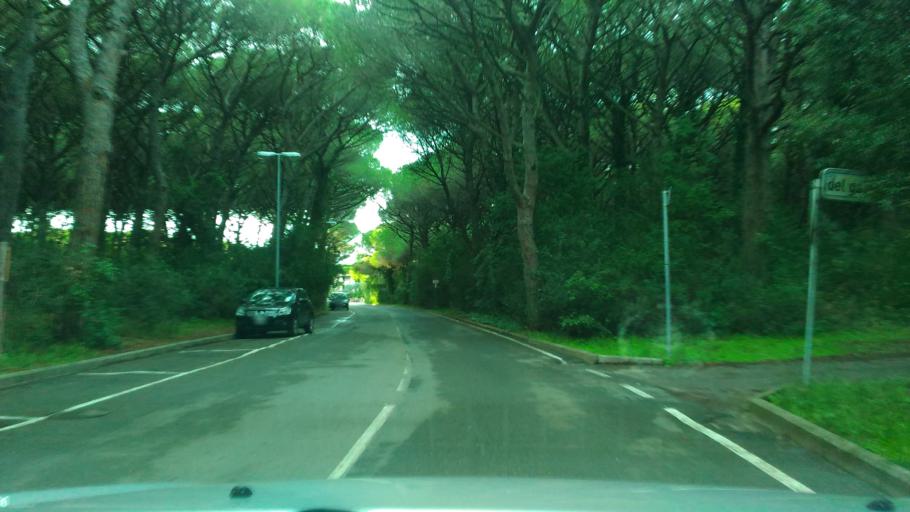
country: IT
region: Tuscany
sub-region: Provincia di Livorno
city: Cecina
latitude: 43.2937
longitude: 10.5041
